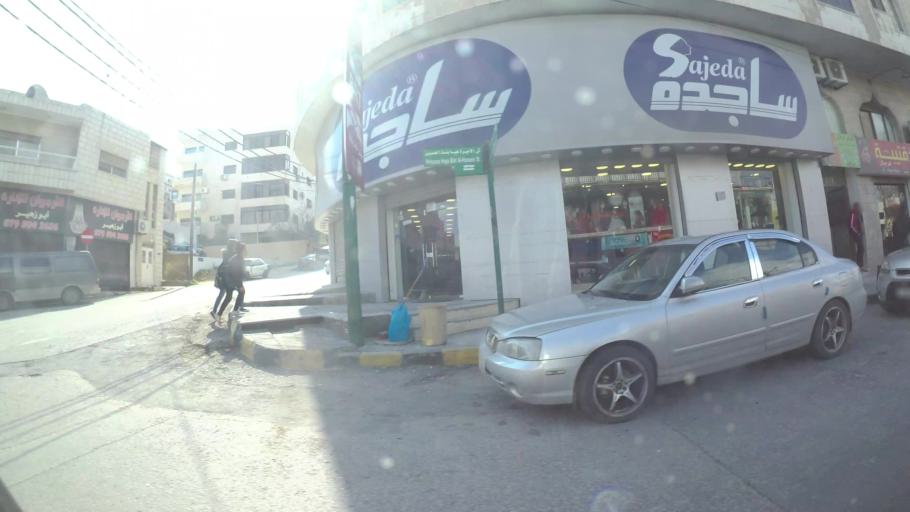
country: JO
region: Amman
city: Al Jubayhah
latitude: 32.0243
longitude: 35.8387
